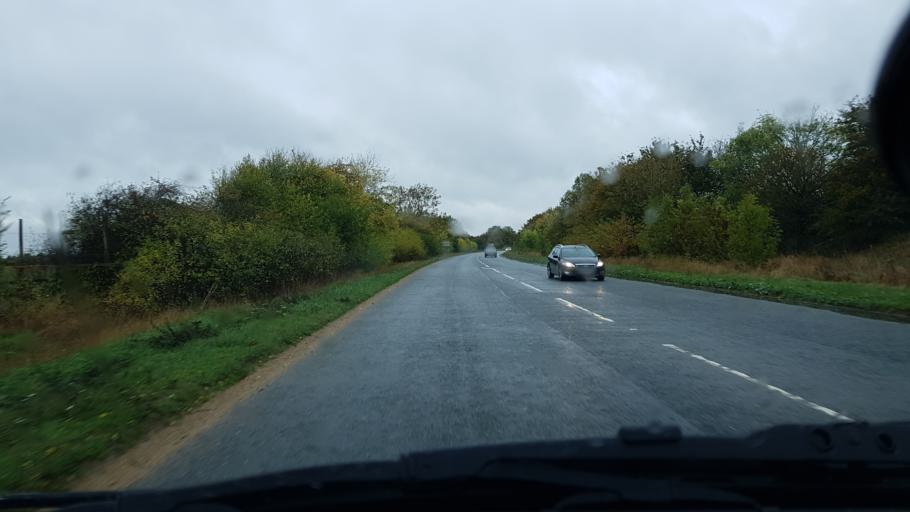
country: GB
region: England
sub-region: Oxfordshire
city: Ducklington
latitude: 51.7652
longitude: -1.4865
